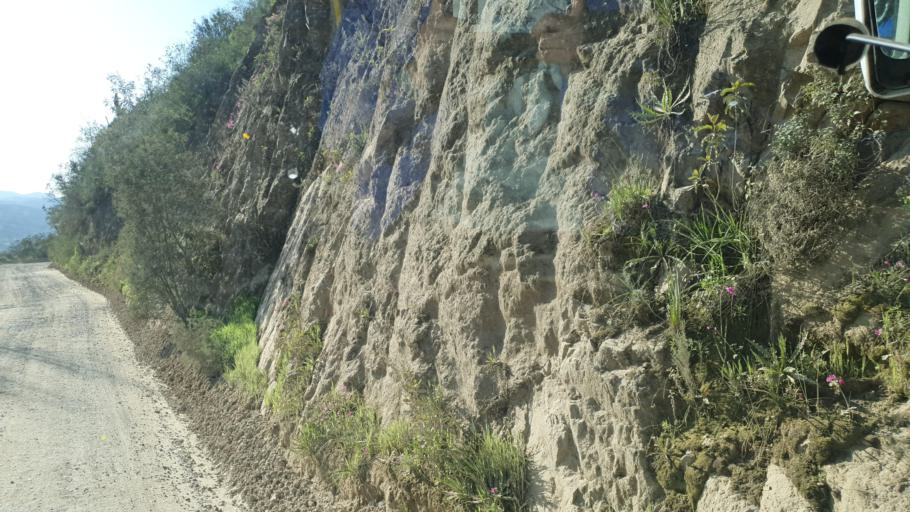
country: CL
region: Valparaiso
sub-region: Provincia de Marga Marga
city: Limache
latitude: -33.2047
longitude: -71.2570
